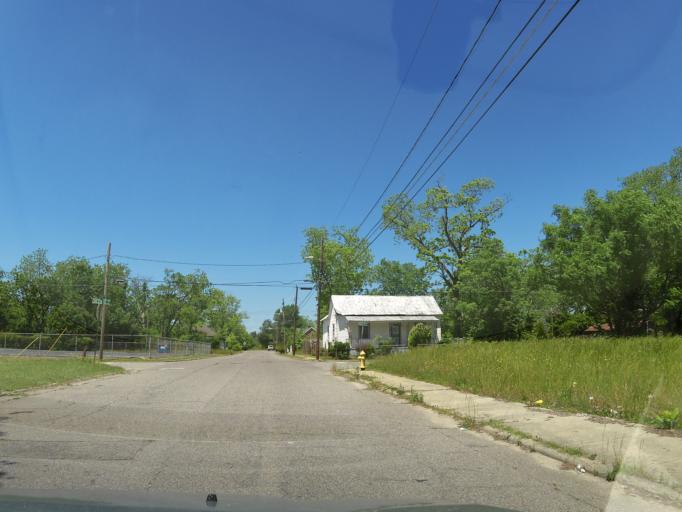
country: US
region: Georgia
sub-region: Richmond County
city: Augusta
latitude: 33.4565
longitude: -81.9845
